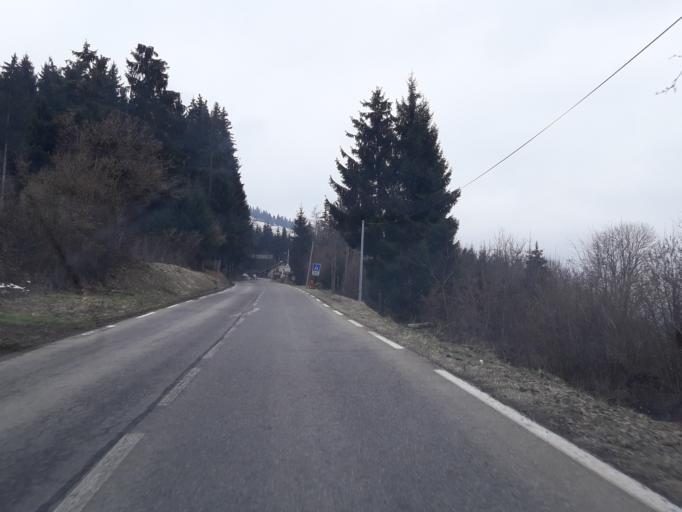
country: FR
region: Rhone-Alpes
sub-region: Departement de l'Isere
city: Theys
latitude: 45.2725
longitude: 5.9884
